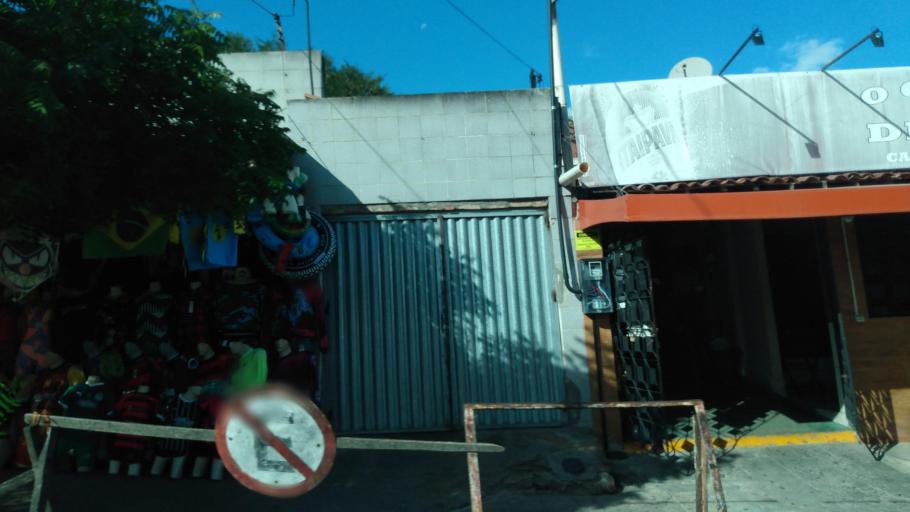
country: ET
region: Oromiya
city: Gore
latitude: 8.1984
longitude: 35.5725
